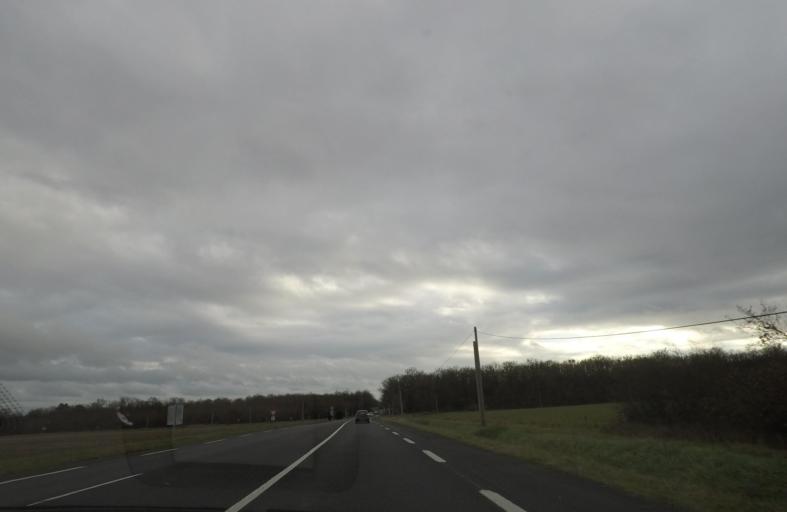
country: FR
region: Centre
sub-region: Departement du Loir-et-Cher
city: Soings-en-Sologne
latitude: 47.4399
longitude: 1.5493
